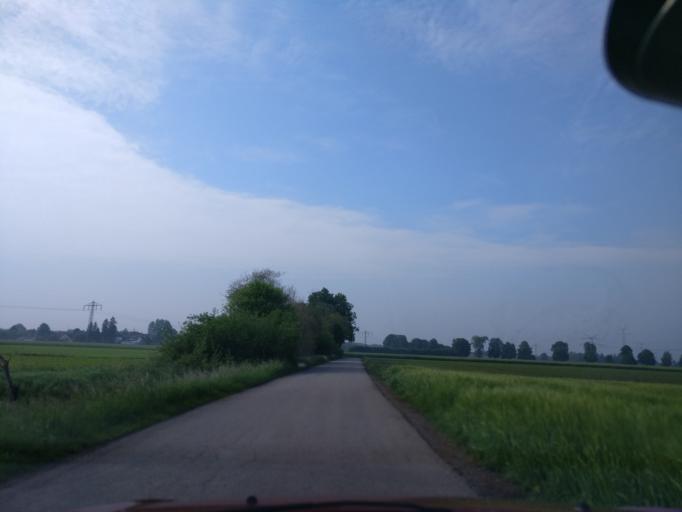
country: DE
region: Bavaria
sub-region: Upper Bavaria
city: Karlsfeld
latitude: 48.2147
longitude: 11.4447
